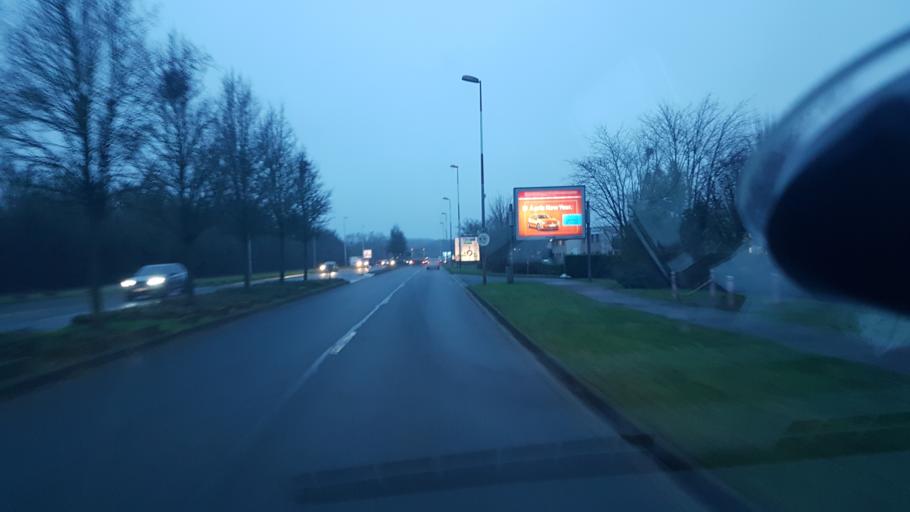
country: FR
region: Ile-de-France
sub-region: Departement de Seine-et-Marne
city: Emerainville
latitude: 48.8184
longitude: 2.6154
